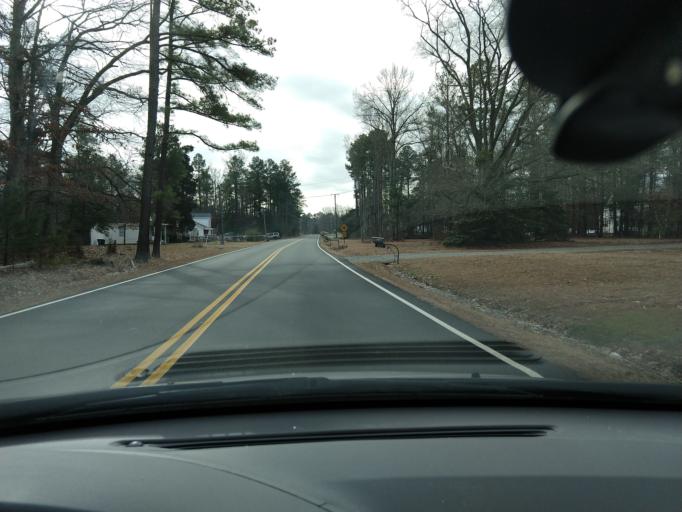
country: US
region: Virginia
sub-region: Henrico County
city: Fort Lee
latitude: 37.4458
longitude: -77.3692
